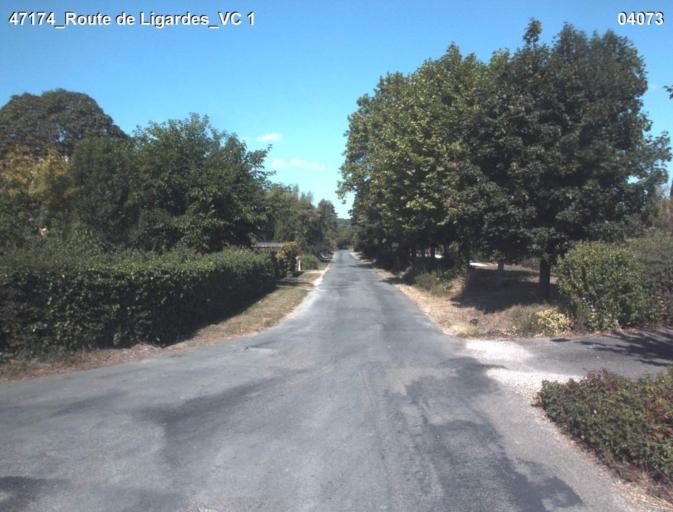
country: FR
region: Midi-Pyrenees
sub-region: Departement du Gers
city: Condom
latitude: 44.0341
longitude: 0.3733
